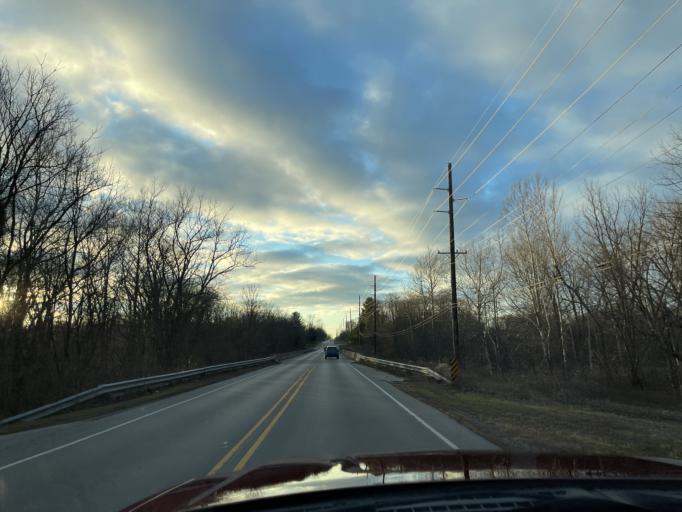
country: US
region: Indiana
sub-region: Hendricks County
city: Avon
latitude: 39.7622
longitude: -86.4438
